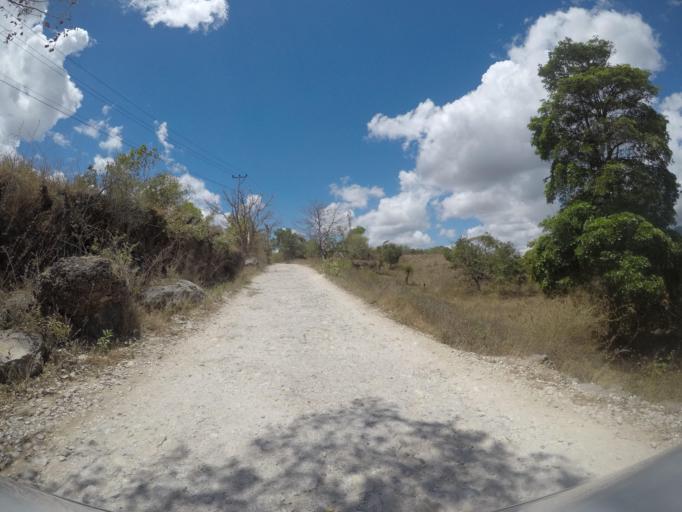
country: TL
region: Baucau
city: Baucau
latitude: -8.4839
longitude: 126.6256
